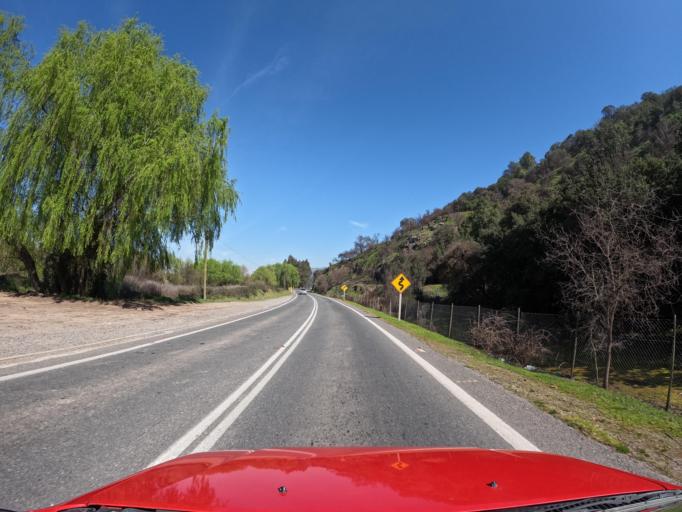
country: CL
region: Maule
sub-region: Provincia de Curico
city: Rauco
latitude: -34.9900
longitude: -71.4323
